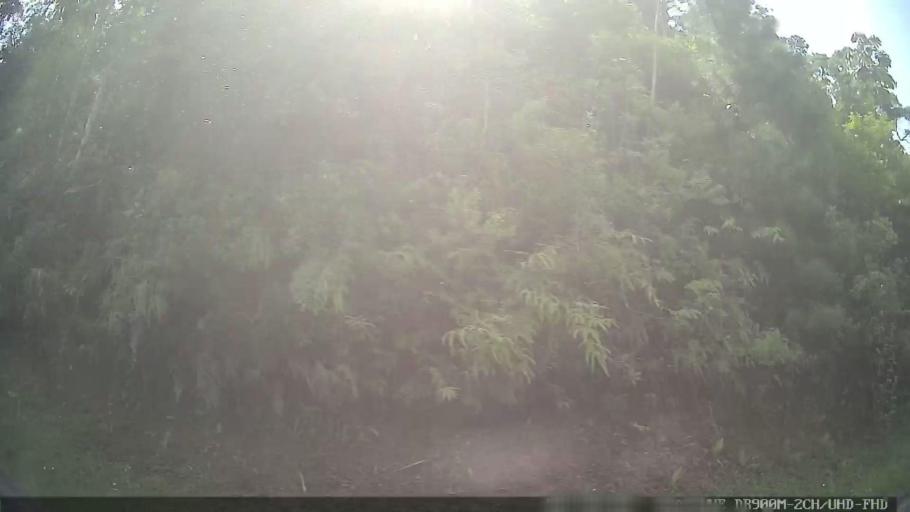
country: BR
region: Sao Paulo
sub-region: Ribeirao Pires
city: Ribeirao Pires
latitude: -23.6780
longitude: -46.3835
